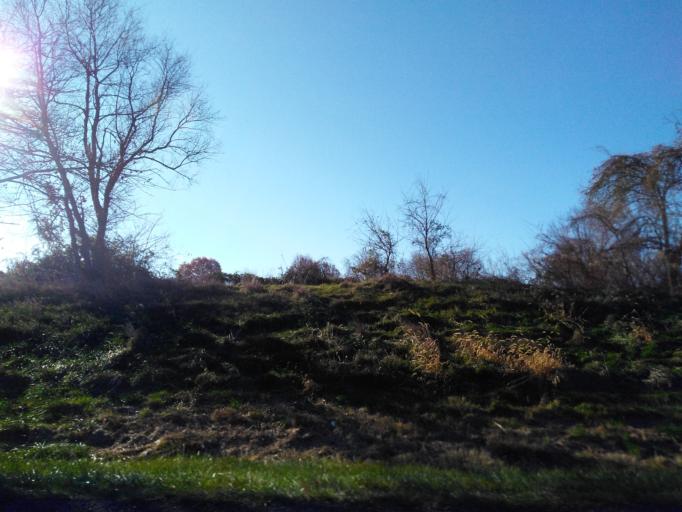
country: US
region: Illinois
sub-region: Madison County
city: Troy
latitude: 38.7555
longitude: -89.8730
